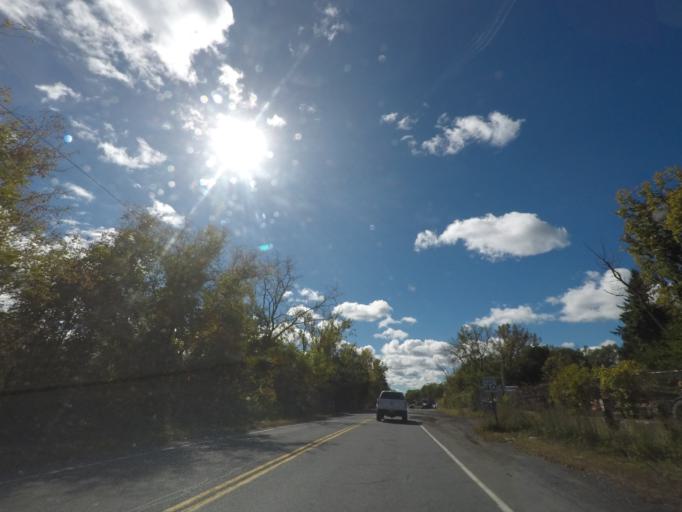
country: US
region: New York
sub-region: Albany County
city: Watervliet
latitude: 42.7198
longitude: -73.7165
